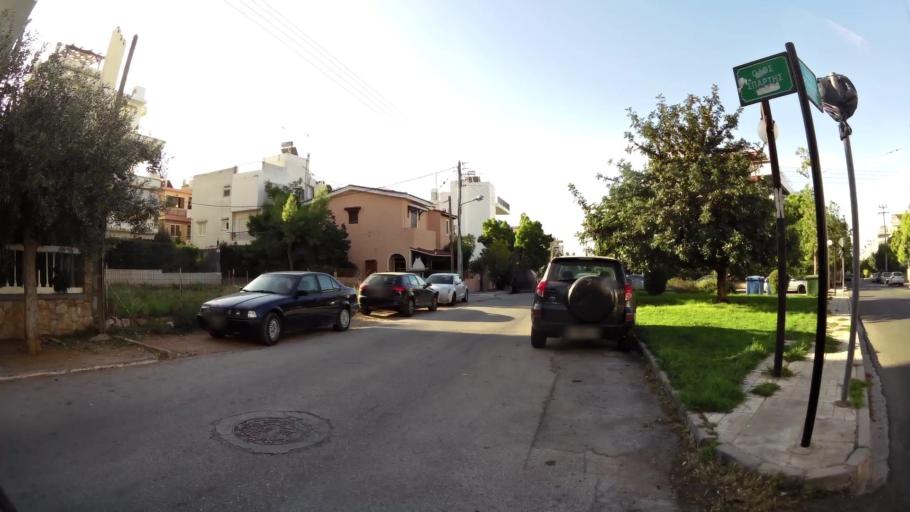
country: GR
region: Attica
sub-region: Nomarchia Athinas
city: Elliniko
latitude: 37.8825
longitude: 23.7499
